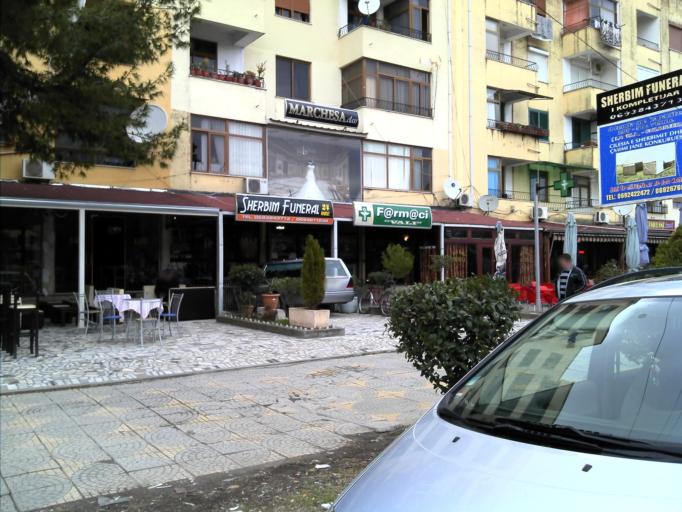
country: AL
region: Shkoder
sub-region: Rrethi i Shkodres
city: Shkoder
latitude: 42.0750
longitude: 19.5239
